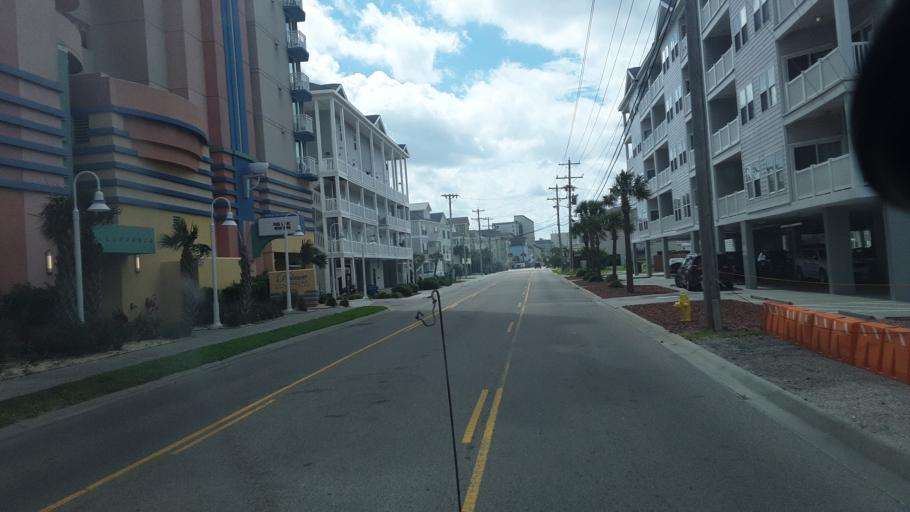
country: US
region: South Carolina
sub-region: Horry County
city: Little River
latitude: 33.8307
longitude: -78.6334
